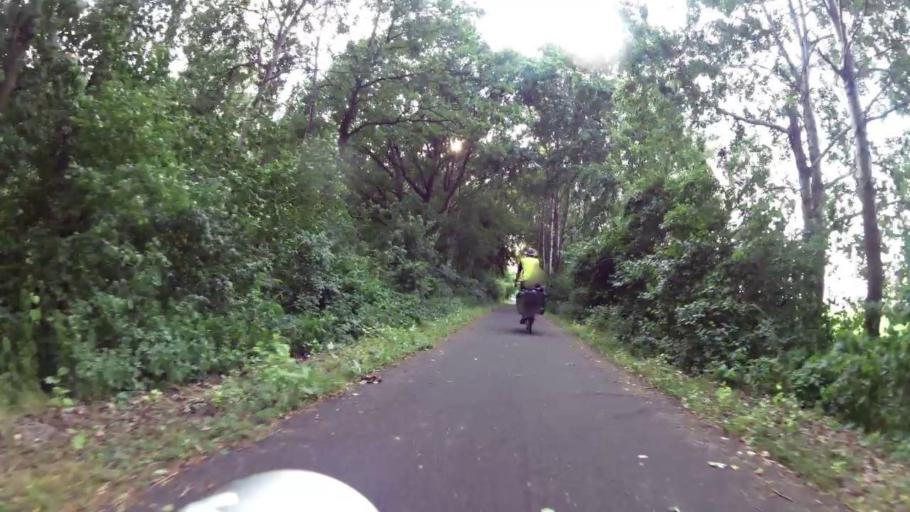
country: PL
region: Kujawsko-Pomorskie
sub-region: Powiat chelminski
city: Unislaw
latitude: 53.1838
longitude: 18.3897
